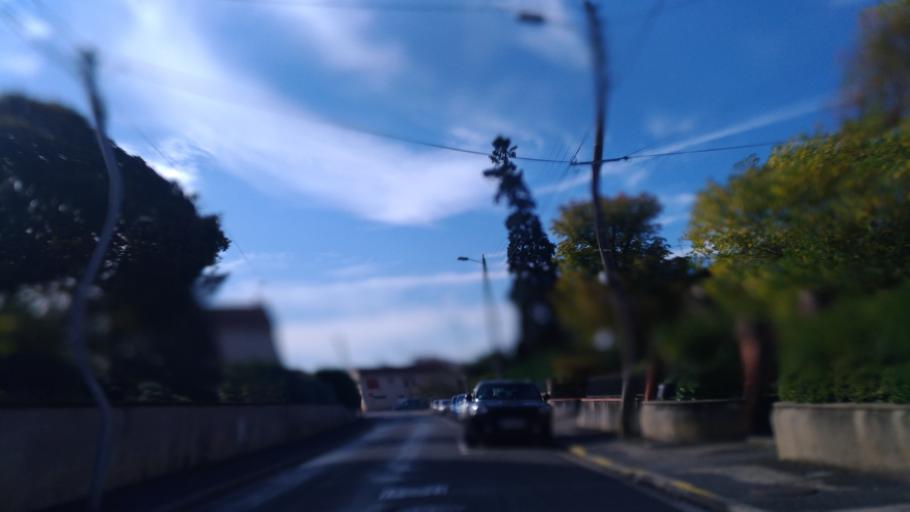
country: FR
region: Midi-Pyrenees
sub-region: Departement du Tarn
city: Albi
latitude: 43.9254
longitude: 2.1338
